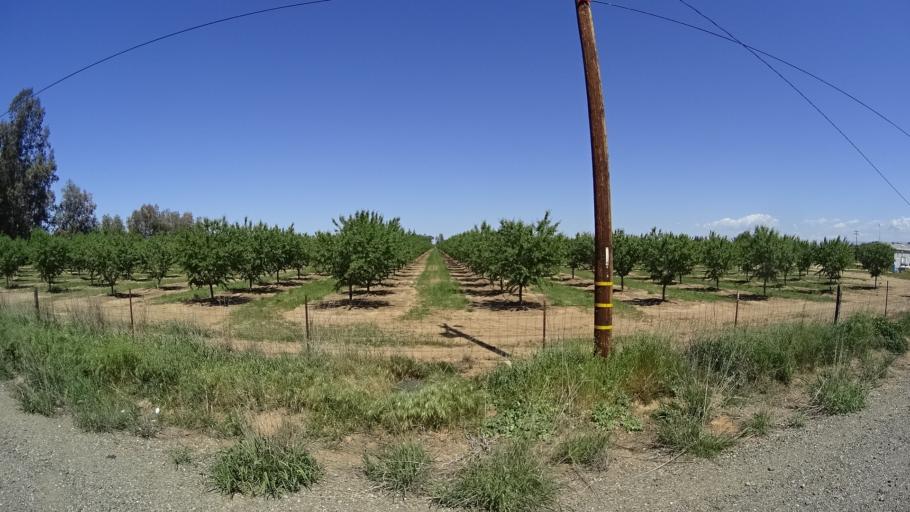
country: US
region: California
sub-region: Glenn County
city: Orland
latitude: 39.7976
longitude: -122.1613
